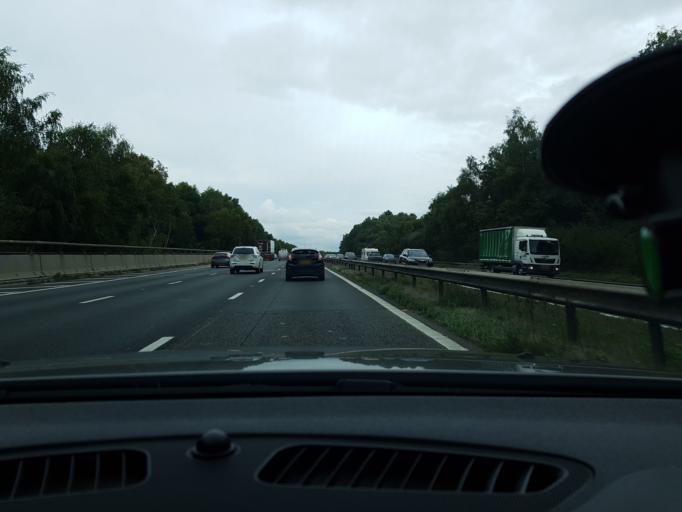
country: GB
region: England
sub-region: Hampshire
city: Odiham
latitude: 51.2828
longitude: -0.9199
